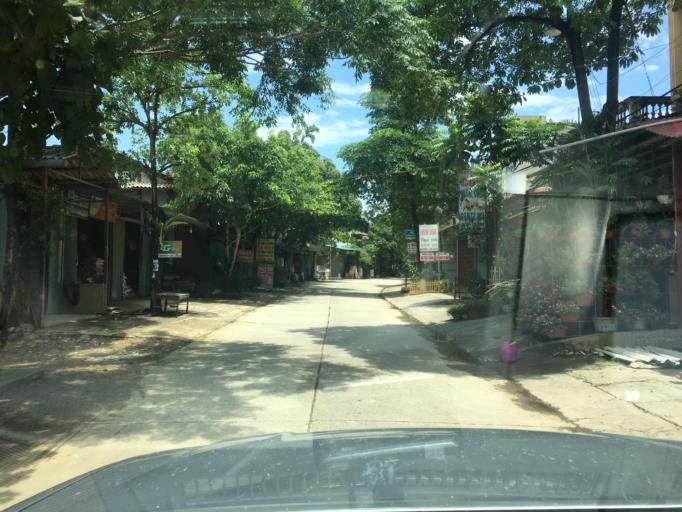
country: VN
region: Yen Bai
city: Son Thinh
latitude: 21.6390
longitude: 104.5023
